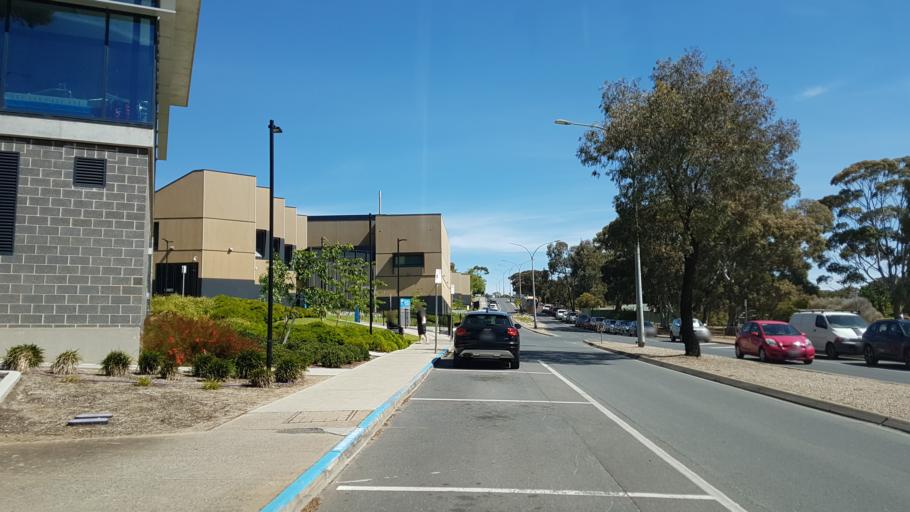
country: AU
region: South Australia
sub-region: Marion
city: Marion
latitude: -35.0228
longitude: 138.5678
